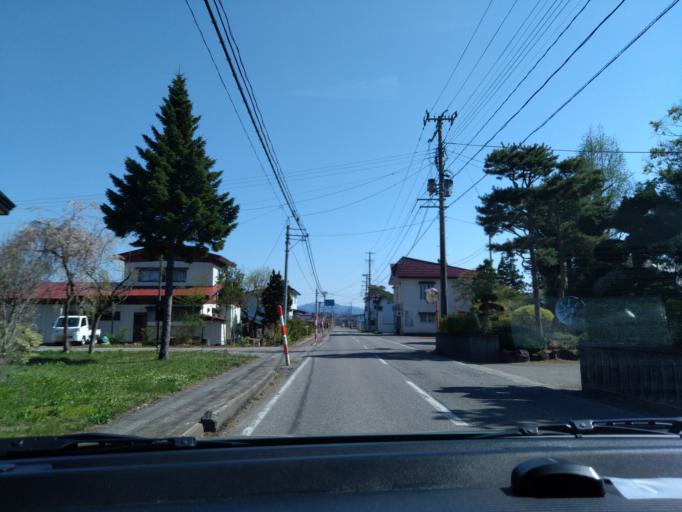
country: JP
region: Akita
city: Kakunodatemachi
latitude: 39.5233
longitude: 140.5878
